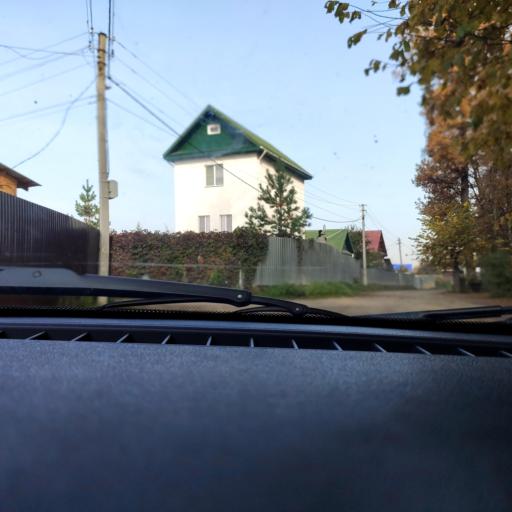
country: RU
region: Bashkortostan
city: Ufa
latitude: 54.6852
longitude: 55.8917
